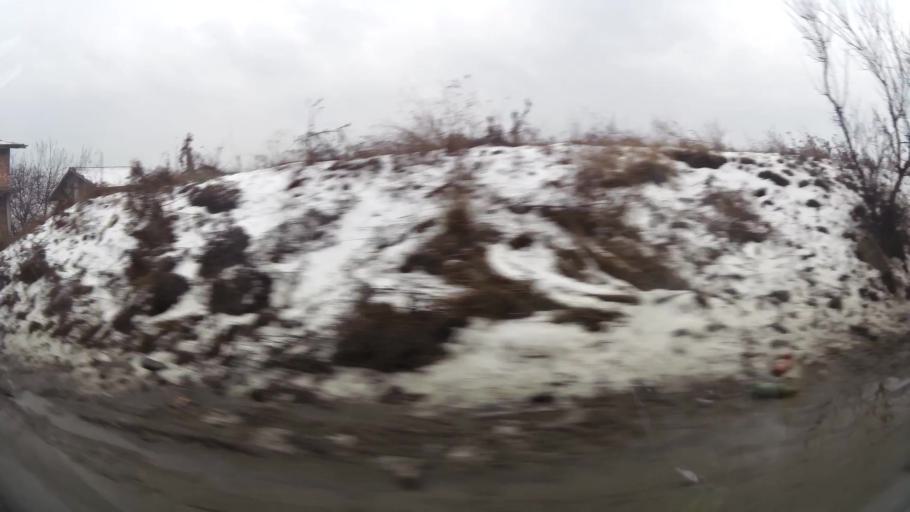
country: BG
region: Sofia-Capital
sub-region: Stolichna Obshtina
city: Sofia
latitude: 42.6952
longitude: 23.2569
